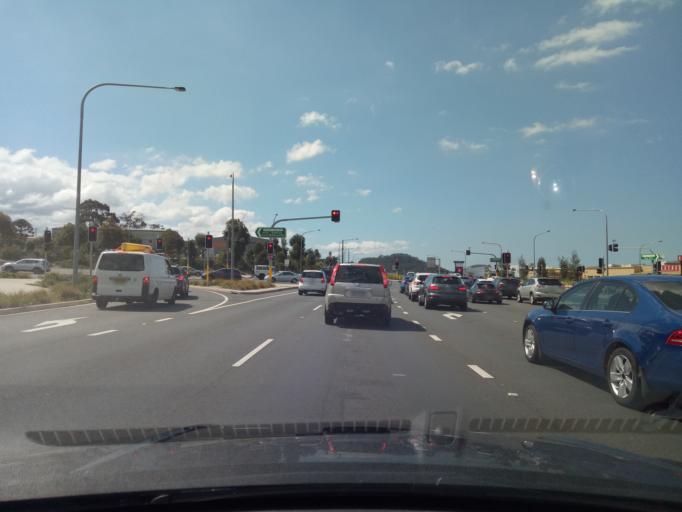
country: AU
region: New South Wales
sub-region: Gosford Shire
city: Point Clare
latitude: -33.4277
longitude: 151.3171
